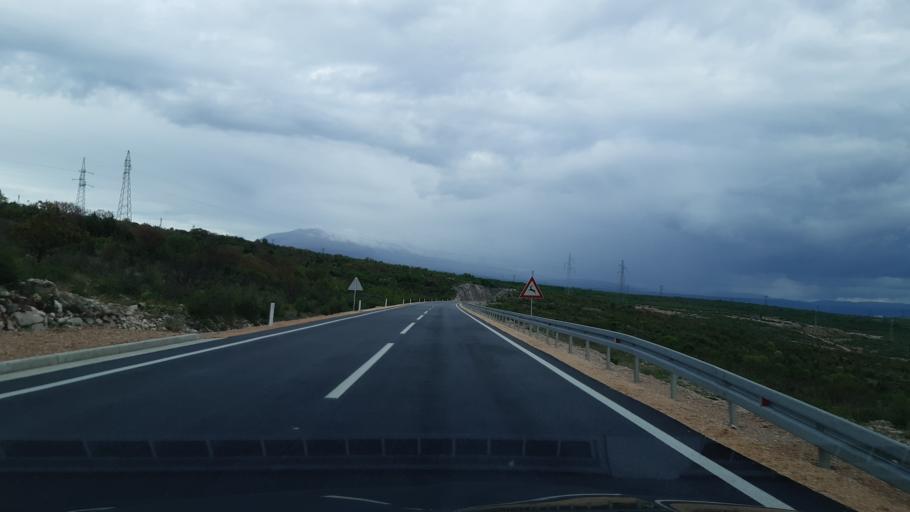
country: BA
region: Federation of Bosnia and Herzegovina
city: Ilici
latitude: 43.3238
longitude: 17.7431
